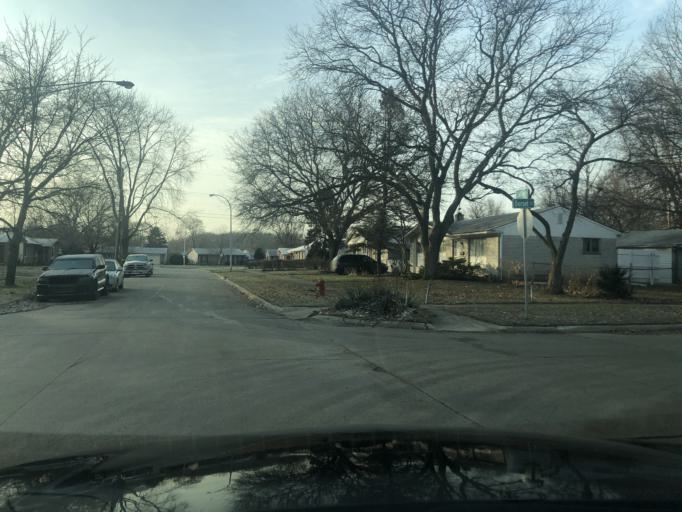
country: US
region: Michigan
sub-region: Wayne County
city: Romulus
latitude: 42.1925
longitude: -83.3331
